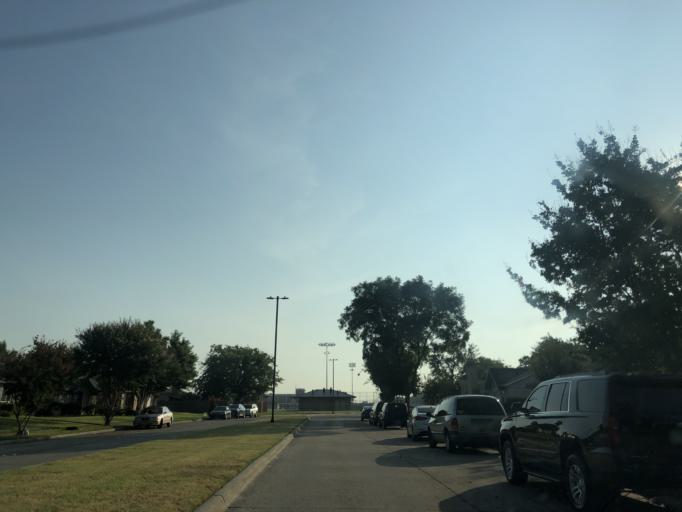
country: US
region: Texas
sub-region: Dallas County
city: Garland
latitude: 32.8693
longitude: -96.6221
